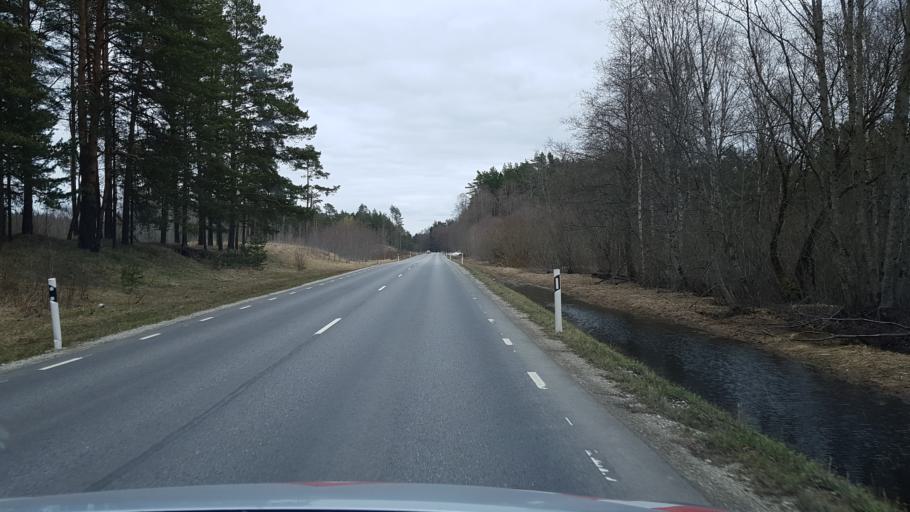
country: EE
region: Ida-Virumaa
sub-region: Narva-Joesuu linn
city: Narva-Joesuu
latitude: 59.4126
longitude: 28.0773
